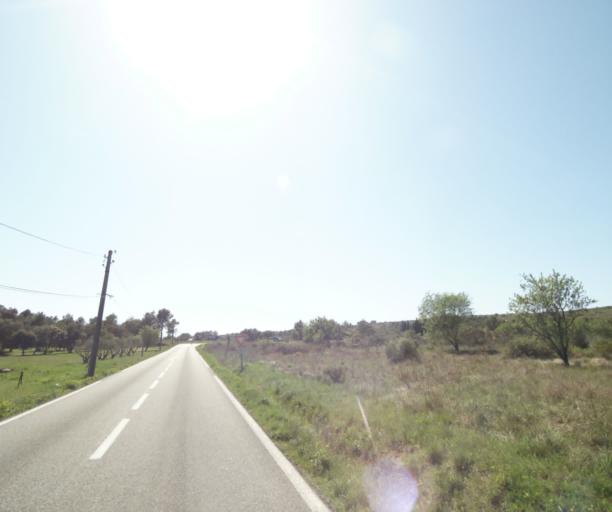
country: FR
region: Languedoc-Roussillon
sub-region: Departement de l'Herault
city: Saint-Drezery
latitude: 43.7239
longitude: 3.9557
